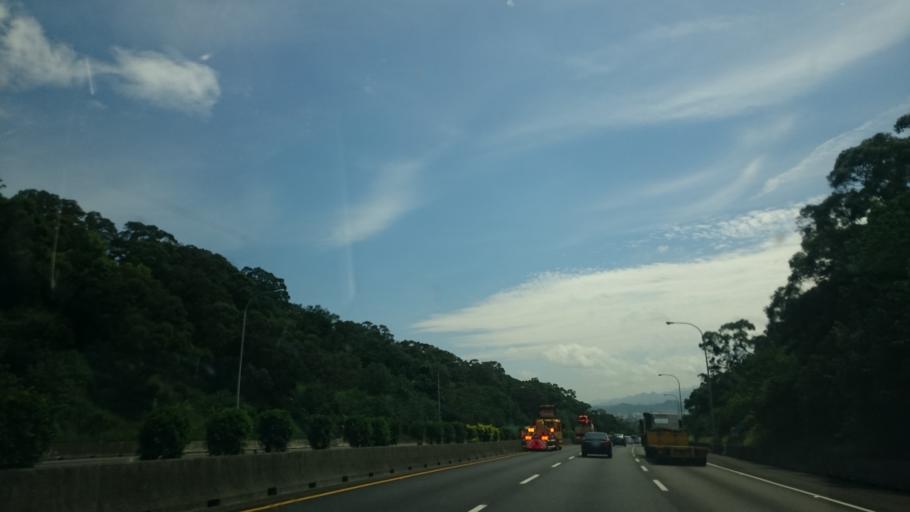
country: TW
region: Taiwan
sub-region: Miaoli
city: Miaoli
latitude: 24.5008
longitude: 120.7888
